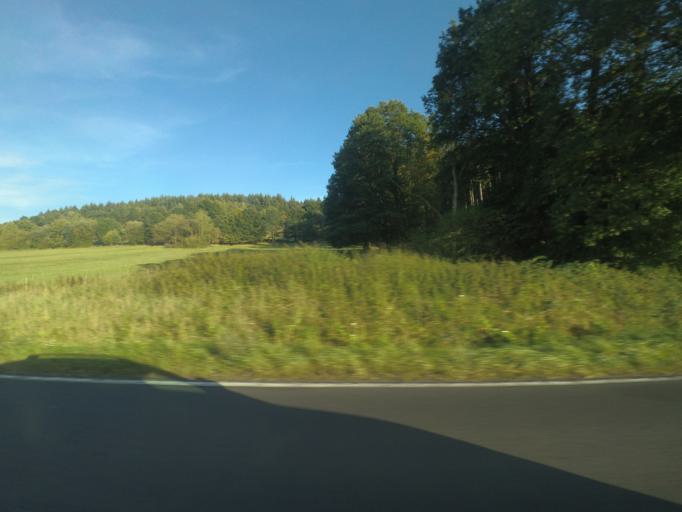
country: DE
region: Hesse
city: Hain-Grundau
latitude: 50.2568
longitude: 9.1752
